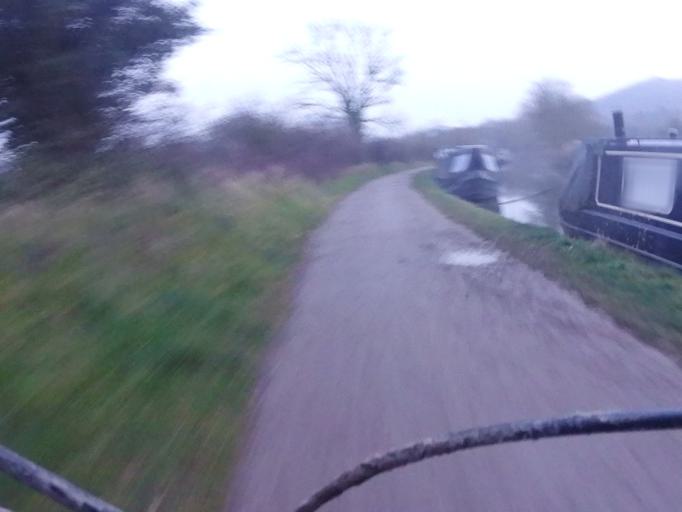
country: GB
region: England
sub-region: Bath and North East Somerset
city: Bath
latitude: 51.3969
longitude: -2.3170
